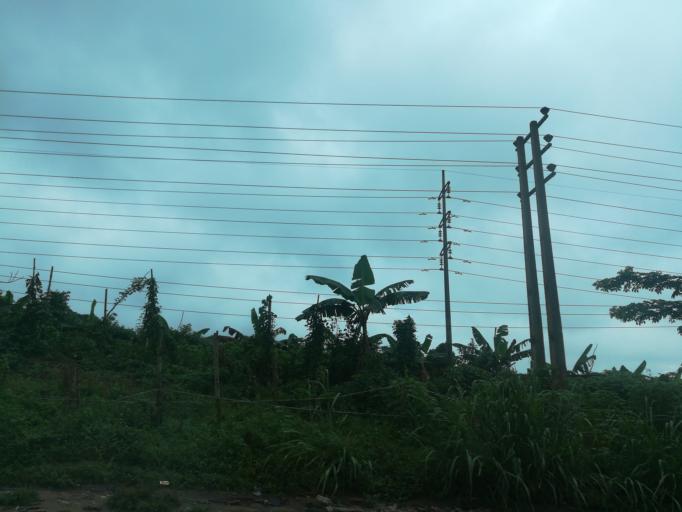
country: NG
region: Lagos
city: Ikorodu
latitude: 6.6449
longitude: 3.5169
